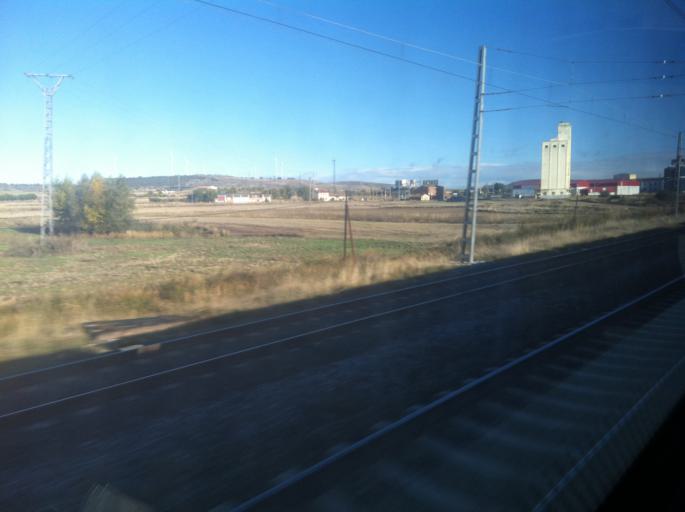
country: ES
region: Castille and Leon
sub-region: Provincia de Burgos
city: Villaquiran de los Infantes
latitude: 42.2126
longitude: -4.0031
